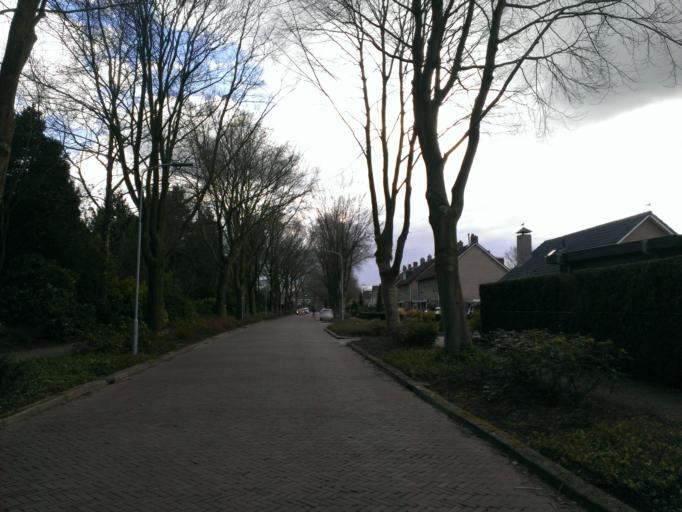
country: NL
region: Gelderland
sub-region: Gemeente Heerde
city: Heerde
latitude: 52.3913
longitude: 6.0330
